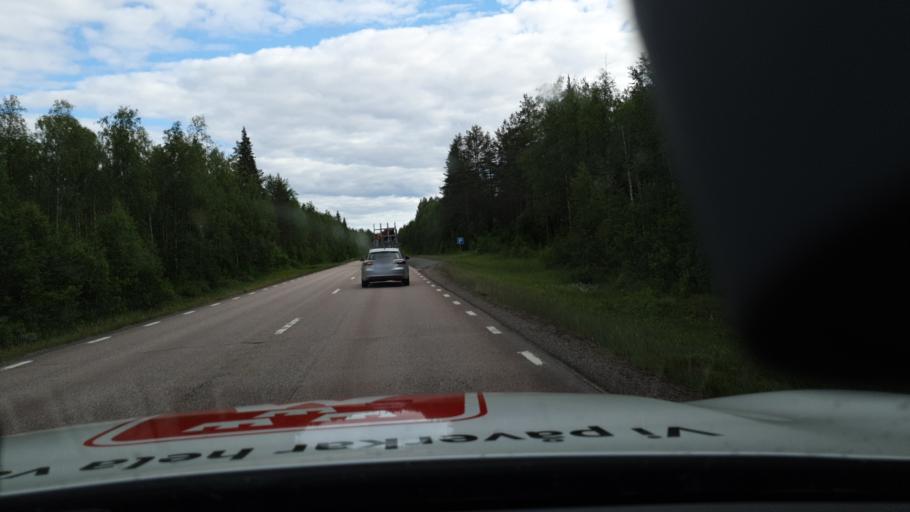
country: SE
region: Norrbotten
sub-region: Kalix Kommun
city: Toere
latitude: 65.9763
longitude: 22.6933
